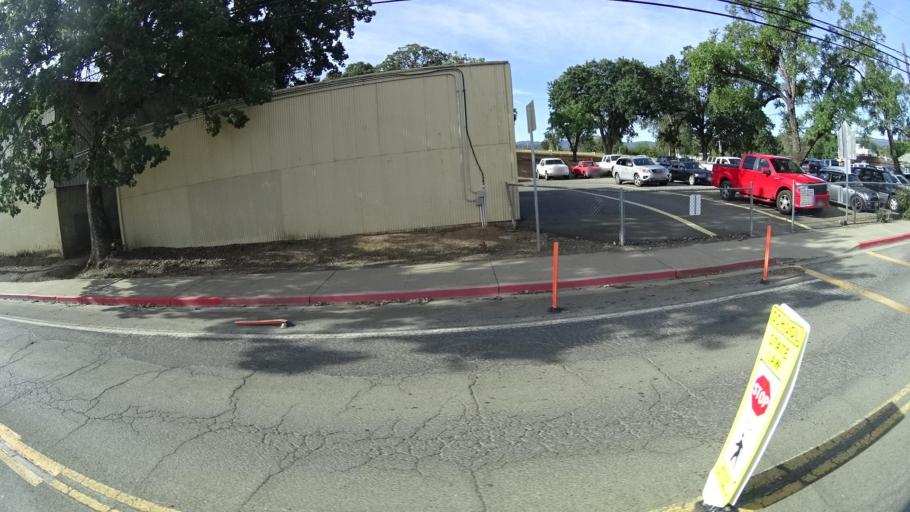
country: US
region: California
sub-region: Lake County
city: Kelseyville
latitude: 38.9756
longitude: -122.8308
